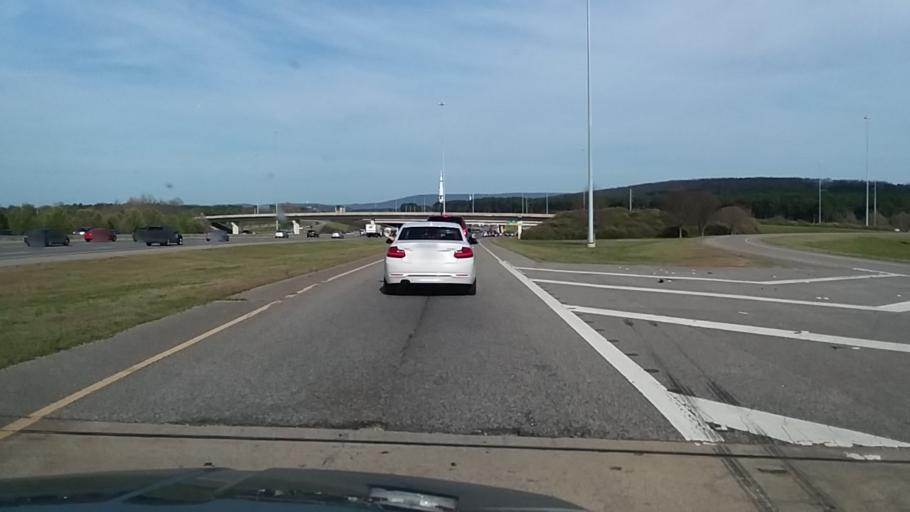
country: US
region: Alabama
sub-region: Madison County
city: Redstone Arsenal
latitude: 34.7055
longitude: -86.6766
